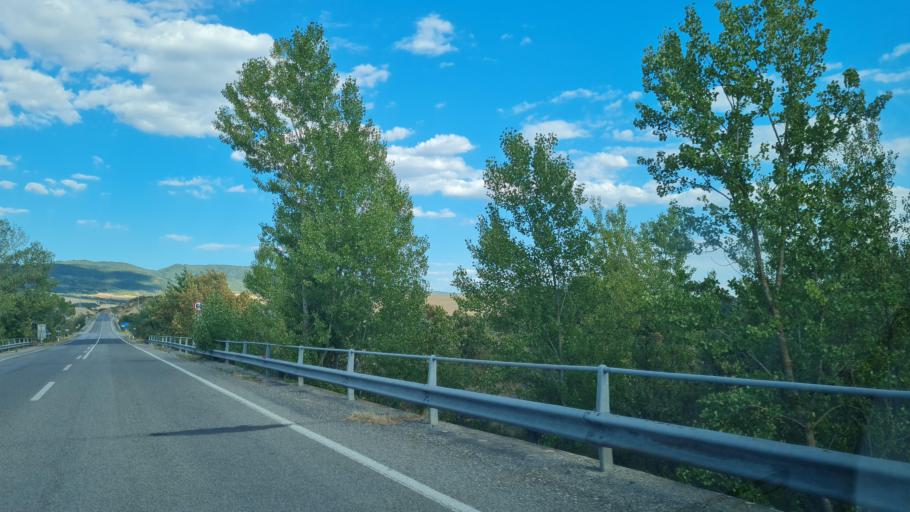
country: IT
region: Tuscany
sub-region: Provincia di Siena
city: Chianciano Terme
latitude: 43.0073
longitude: 11.7396
